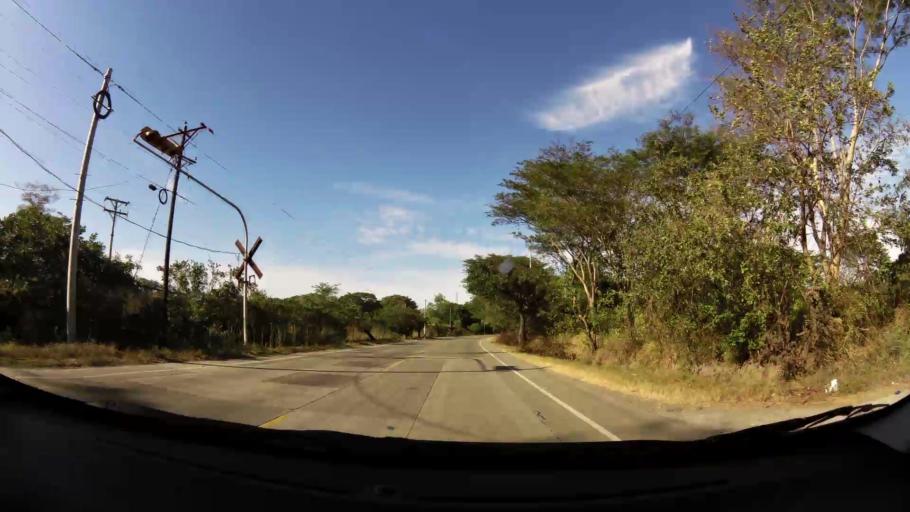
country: SV
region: Santa Ana
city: Texistepeque
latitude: 14.1019
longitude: -89.5000
